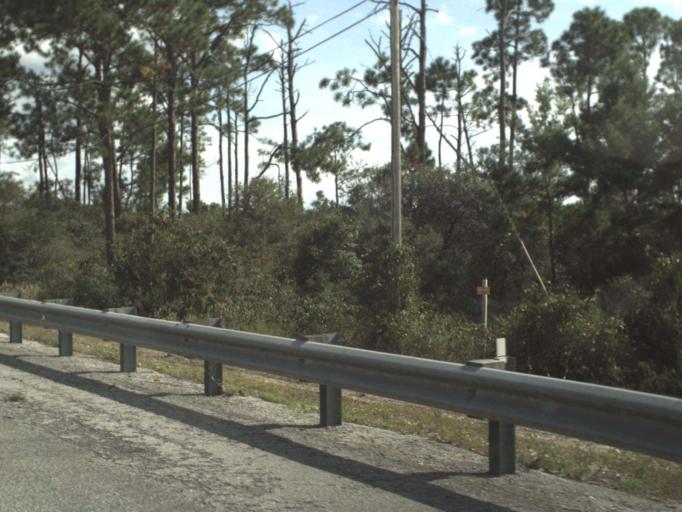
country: US
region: Florida
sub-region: Bay County
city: Mexico Beach
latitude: 29.9556
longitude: -85.4308
